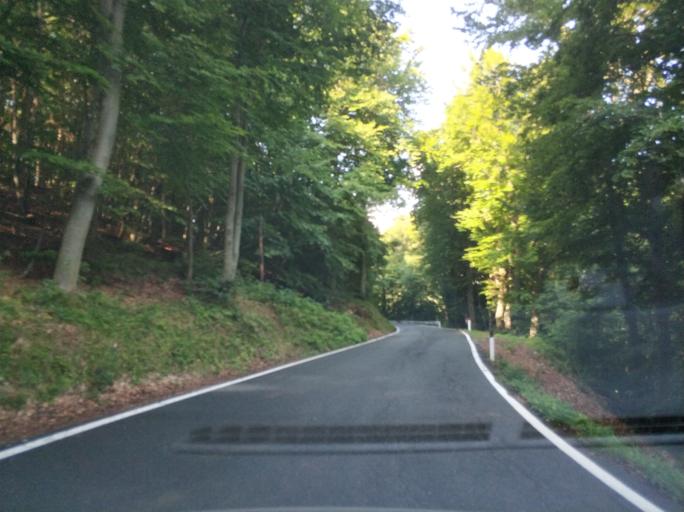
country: IT
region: Piedmont
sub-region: Provincia di Torino
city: Viu
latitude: 45.2214
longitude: 7.3860
